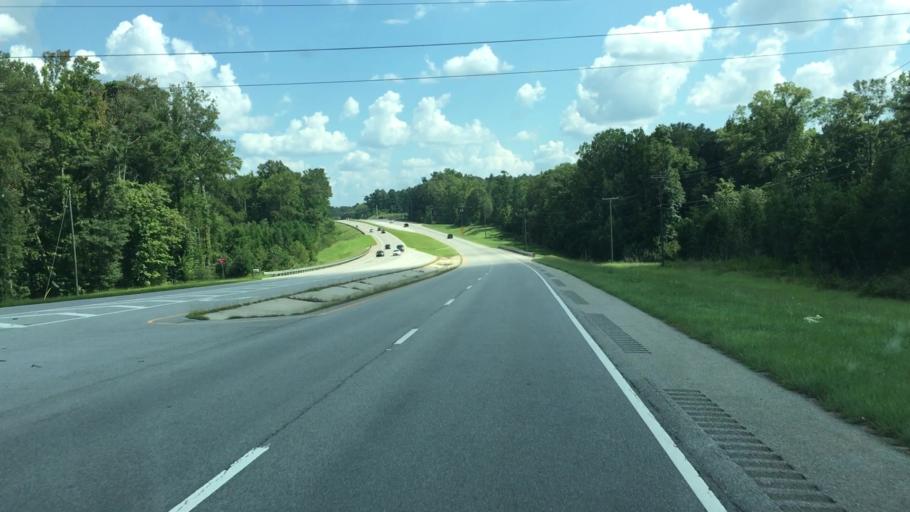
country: US
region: Georgia
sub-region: Putnam County
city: Eatonton
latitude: 33.2426
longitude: -83.3231
